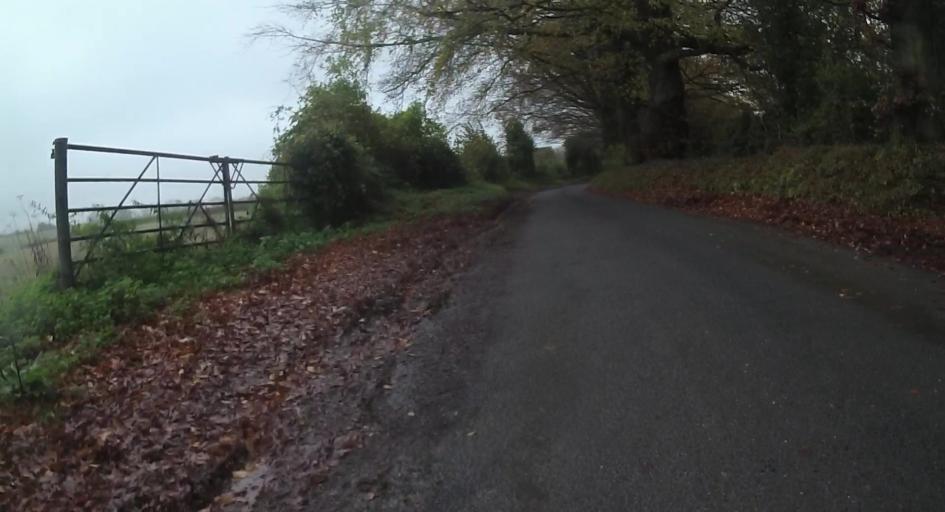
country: GB
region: England
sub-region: Hampshire
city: Four Marks
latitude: 51.1496
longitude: -1.1155
